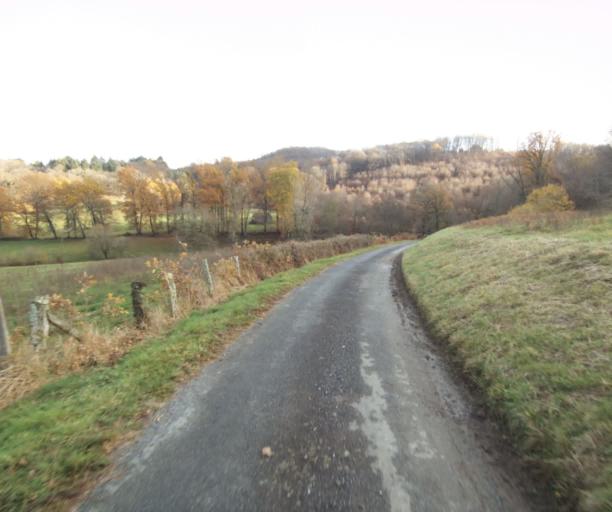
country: FR
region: Limousin
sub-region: Departement de la Correze
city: Cornil
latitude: 45.1971
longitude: 1.6956
